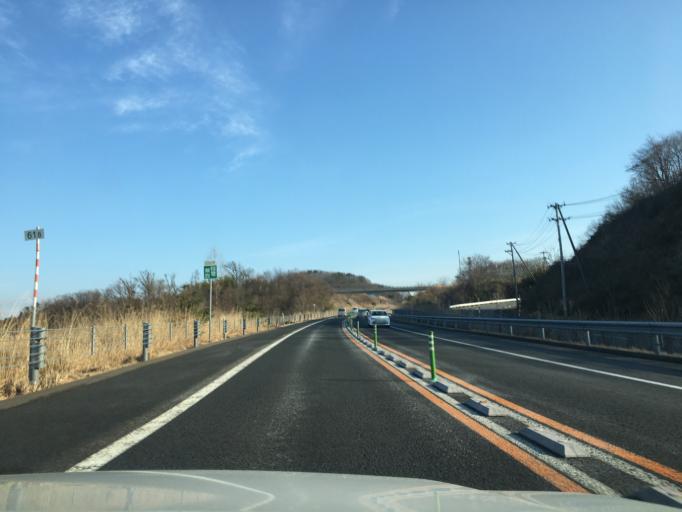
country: JP
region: Yamagata
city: Sagae
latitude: 38.3991
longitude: 140.2102
